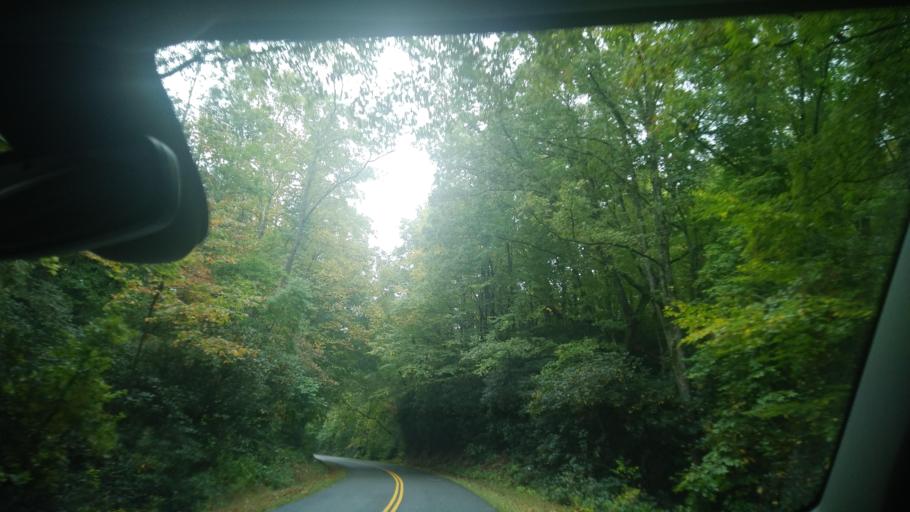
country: US
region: North Carolina
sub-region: Mitchell County
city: Spruce Pine
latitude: 35.8779
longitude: -82.0028
